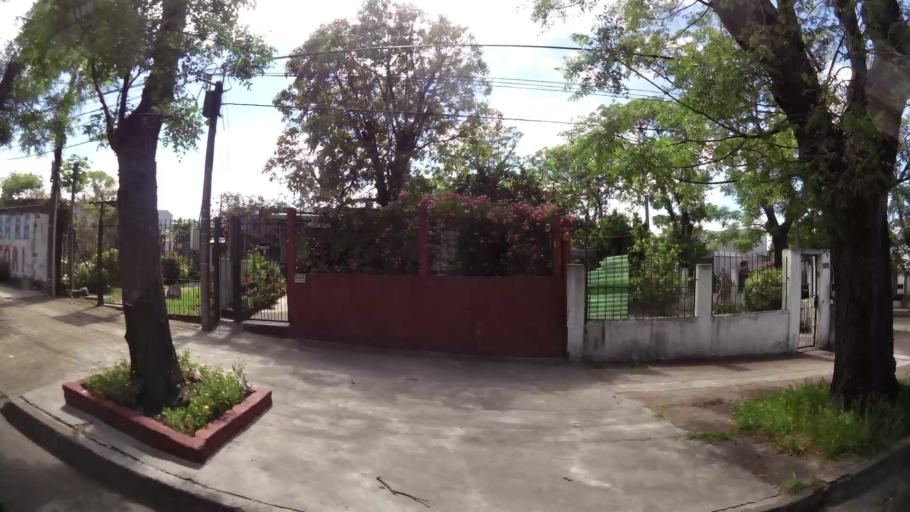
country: UY
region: Montevideo
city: Montevideo
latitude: -34.8544
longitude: -56.1443
